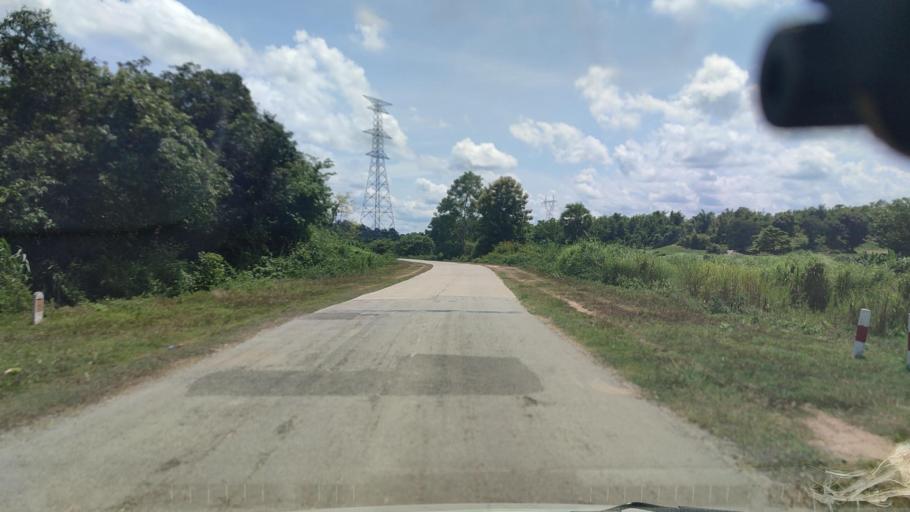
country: MM
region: Mandalay
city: Nay Pyi Taw
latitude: 19.9396
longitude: 95.9786
